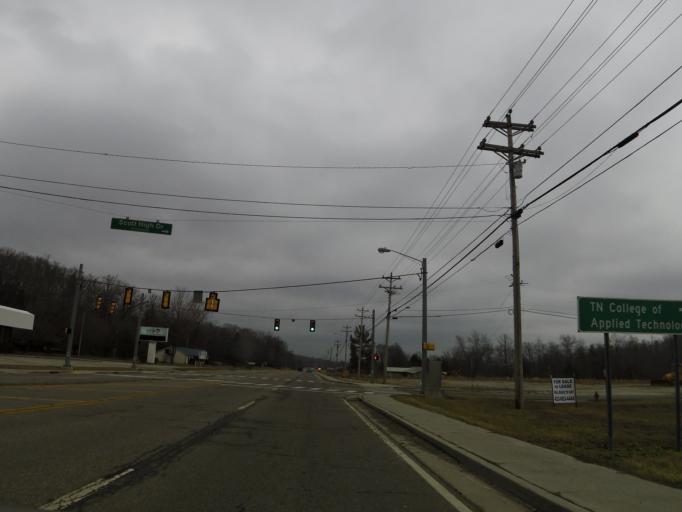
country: US
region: Tennessee
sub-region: Scott County
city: Huntsville
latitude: 36.4124
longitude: -84.5298
